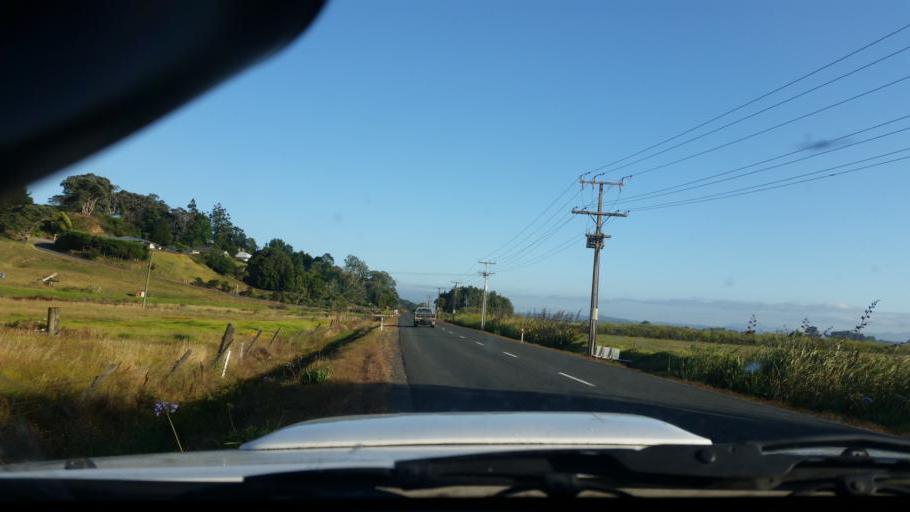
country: NZ
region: Northland
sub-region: Kaipara District
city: Dargaville
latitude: -35.9738
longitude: 173.8743
